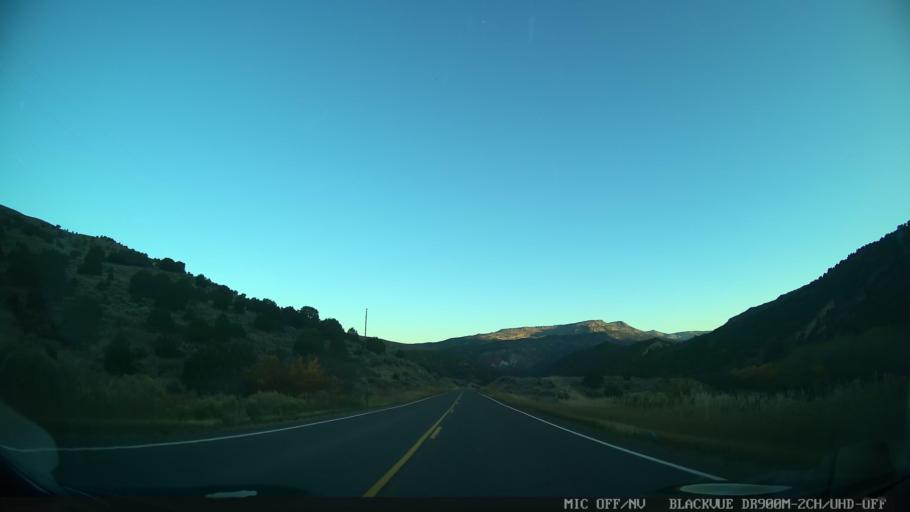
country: US
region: Colorado
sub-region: Eagle County
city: Edwards
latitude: 39.8368
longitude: -106.6394
